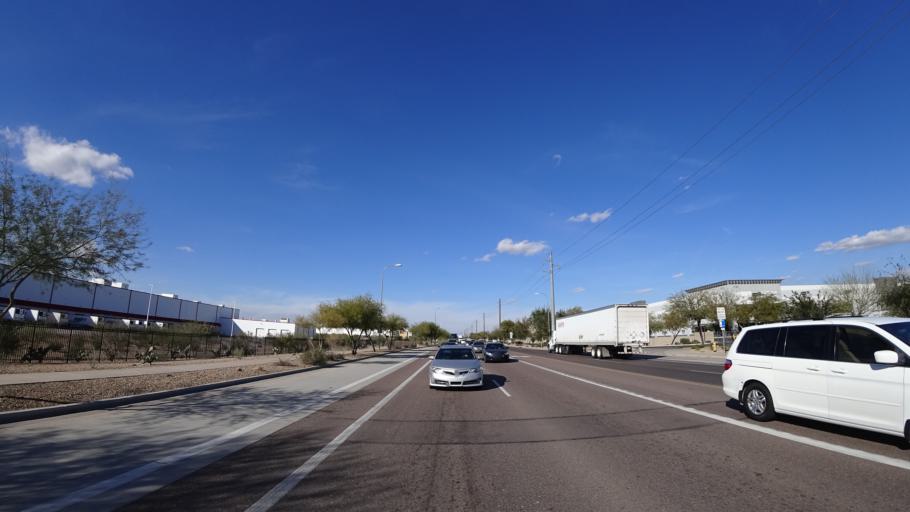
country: US
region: Arizona
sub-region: Maricopa County
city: Tolleson
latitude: 33.4305
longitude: -112.2212
